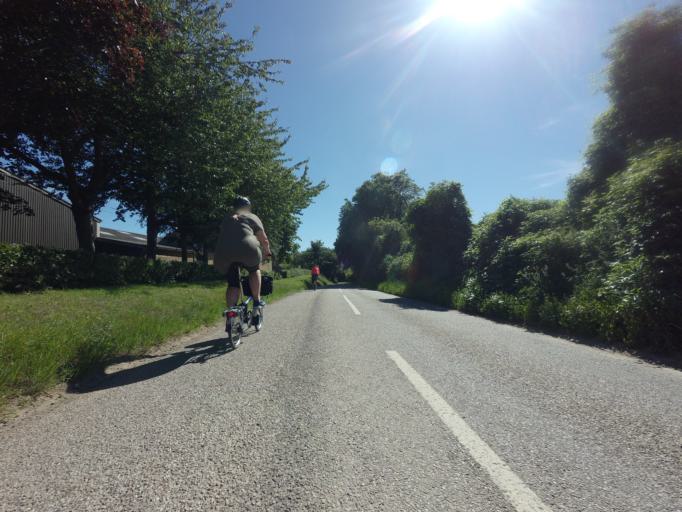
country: GB
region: England
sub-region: Kent
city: Birchington-on-Sea
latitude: 51.3331
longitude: 1.3215
